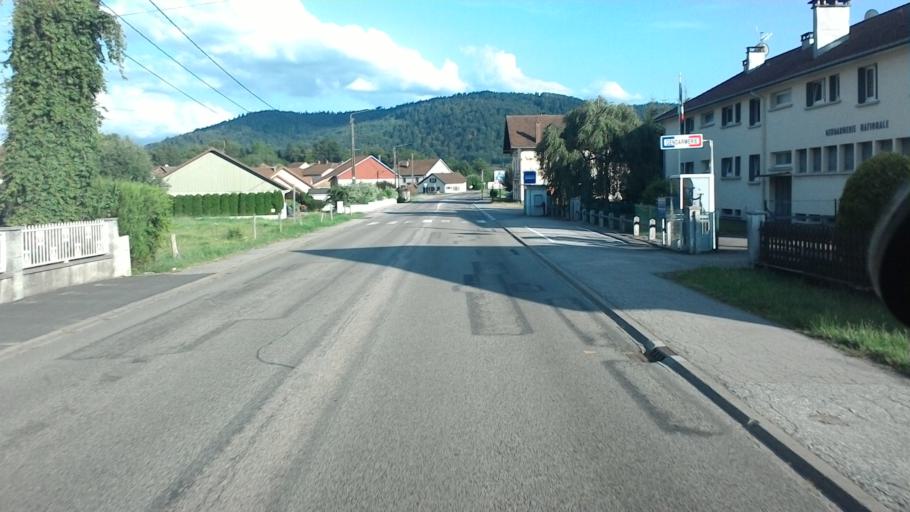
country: FR
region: Lorraine
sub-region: Departement des Vosges
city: Rupt-sur-Moselle
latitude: 47.9162
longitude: 6.6660
